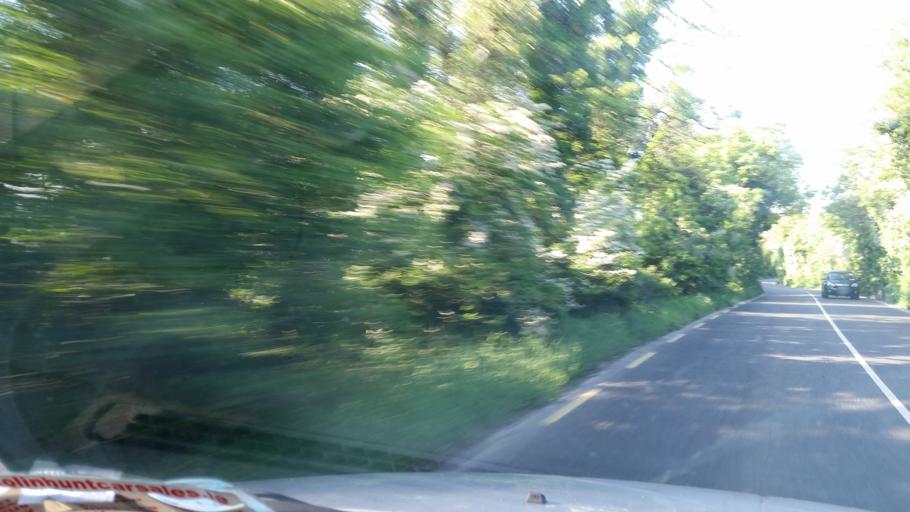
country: IE
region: Leinster
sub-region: Fingal County
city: Blanchardstown
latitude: 53.4193
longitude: -6.3418
